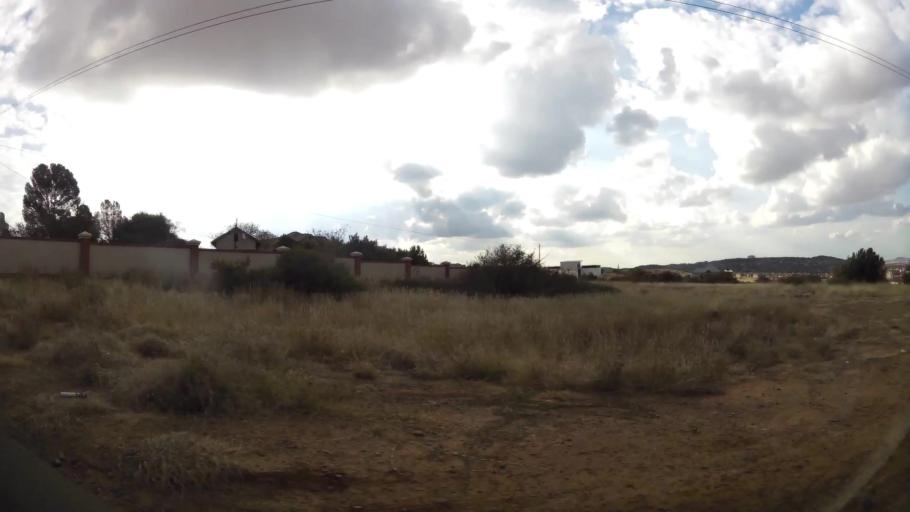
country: ZA
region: Orange Free State
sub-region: Mangaung Metropolitan Municipality
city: Bloemfontein
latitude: -29.0696
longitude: 26.1982
